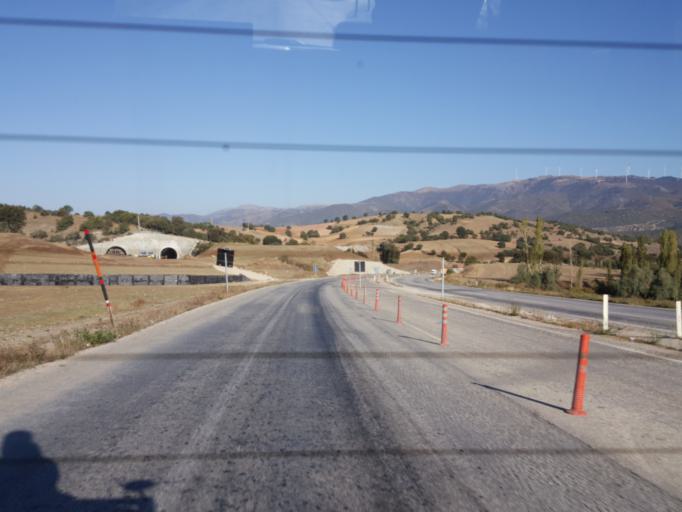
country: TR
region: Amasya
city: Ezinepazari
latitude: 40.5535
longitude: 36.1404
